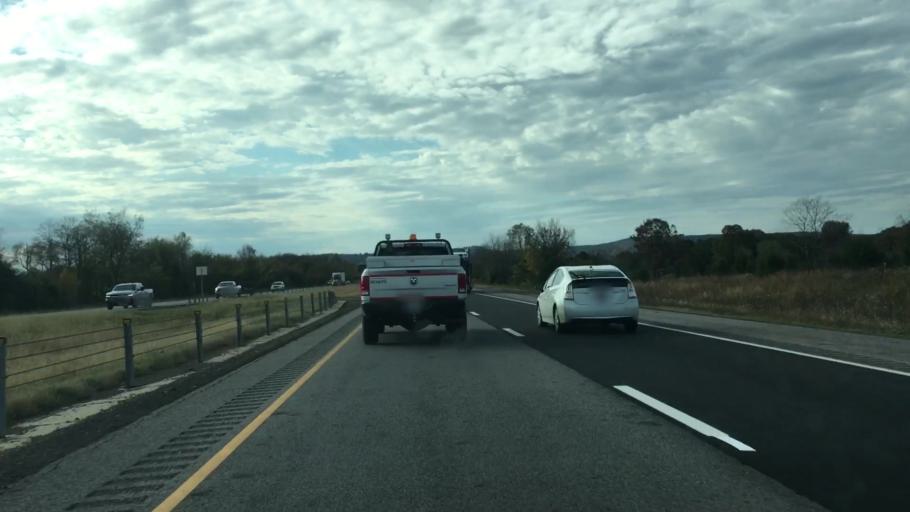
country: US
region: Arkansas
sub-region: Pope County
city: Atkins
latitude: 35.2493
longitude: -92.8807
